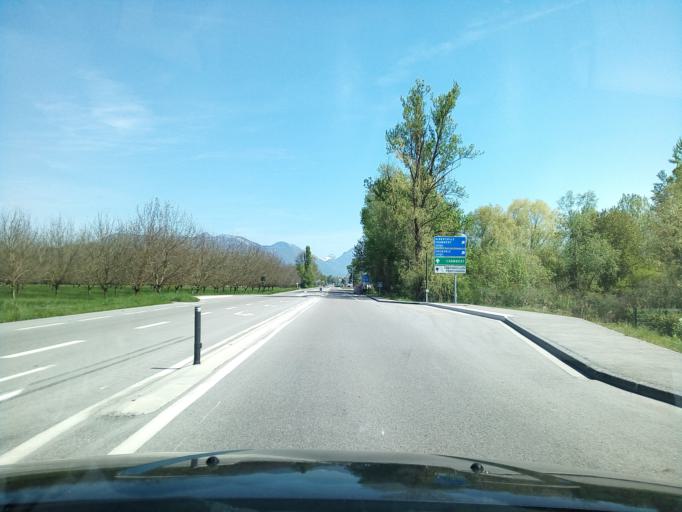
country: FR
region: Rhone-Alpes
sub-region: Departement de l'Isere
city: Barraux
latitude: 45.4245
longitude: 5.9922
